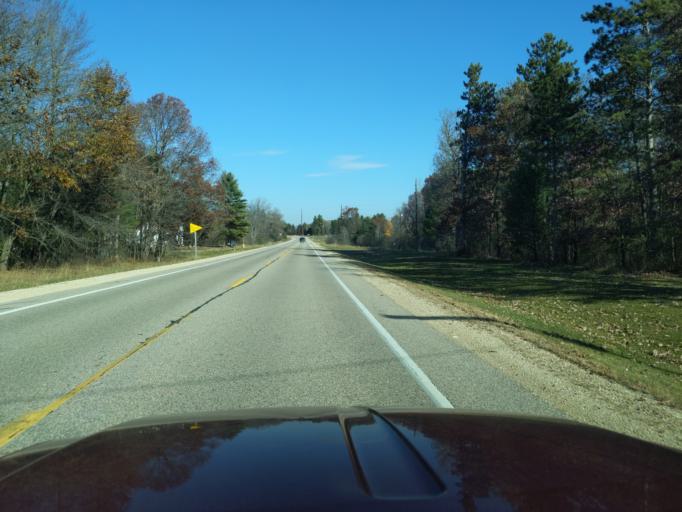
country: US
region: Wisconsin
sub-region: Waushara County
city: Wautoma
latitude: 44.0506
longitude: -89.2942
